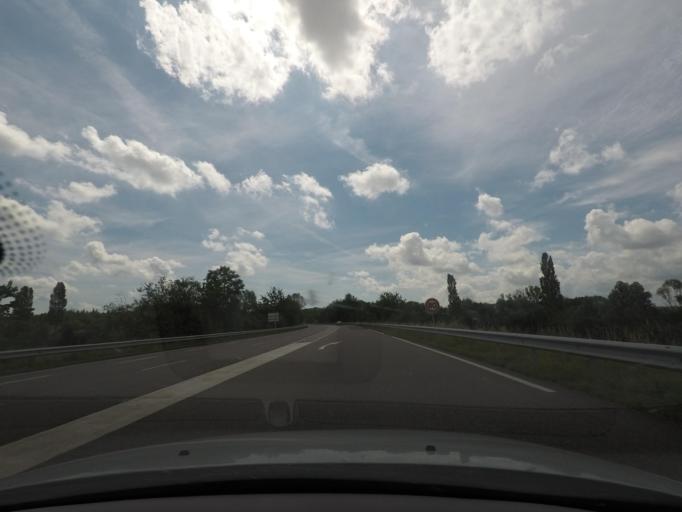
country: FR
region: Alsace
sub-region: Departement du Bas-Rhin
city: Drulingen
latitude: 48.8629
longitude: 7.1815
